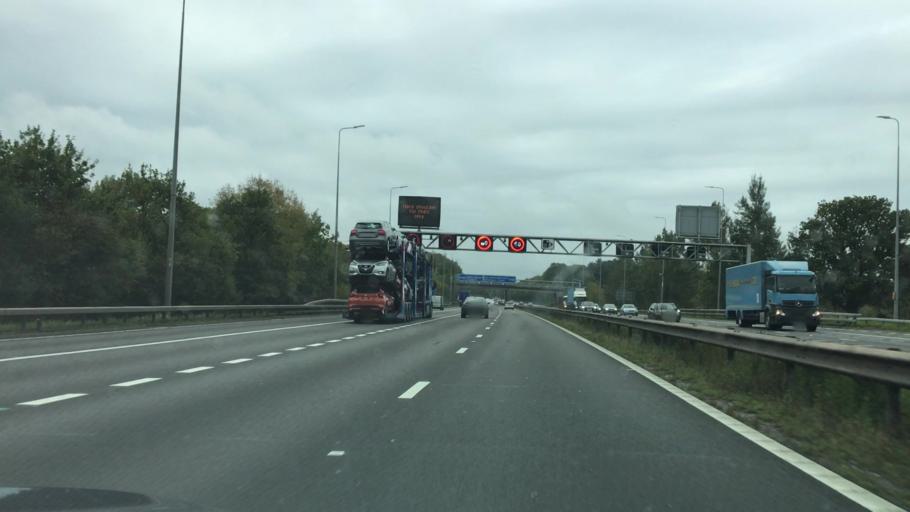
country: GB
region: England
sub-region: Solihull
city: Cheswick Green
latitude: 52.3590
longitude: -1.8070
